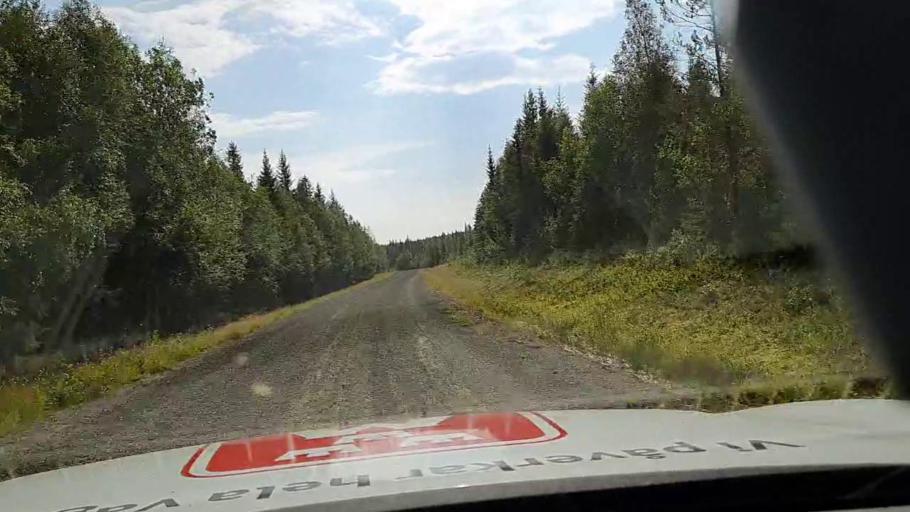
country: SE
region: Vaesterbotten
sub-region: Storumans Kommun
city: Fristad
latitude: 65.5425
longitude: 16.7974
